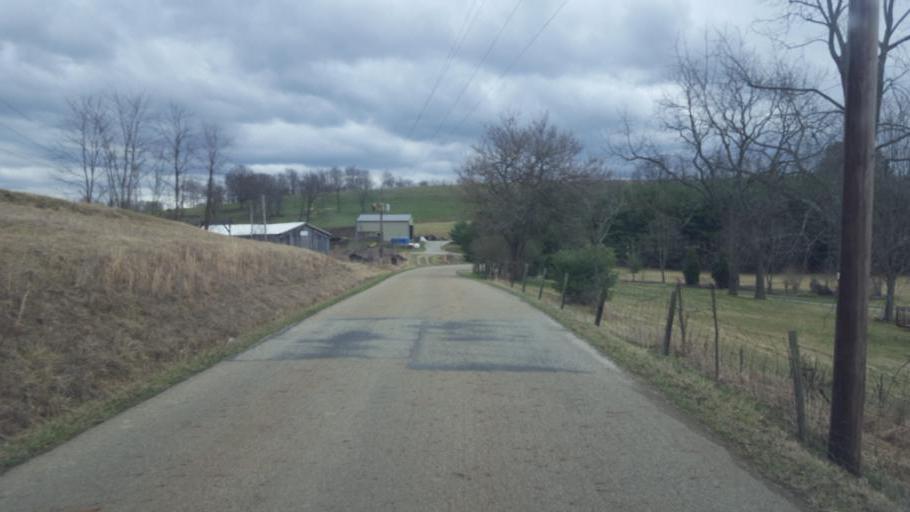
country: US
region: Ohio
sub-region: Muskingum County
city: Frazeysburg
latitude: 40.1361
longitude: -82.2288
